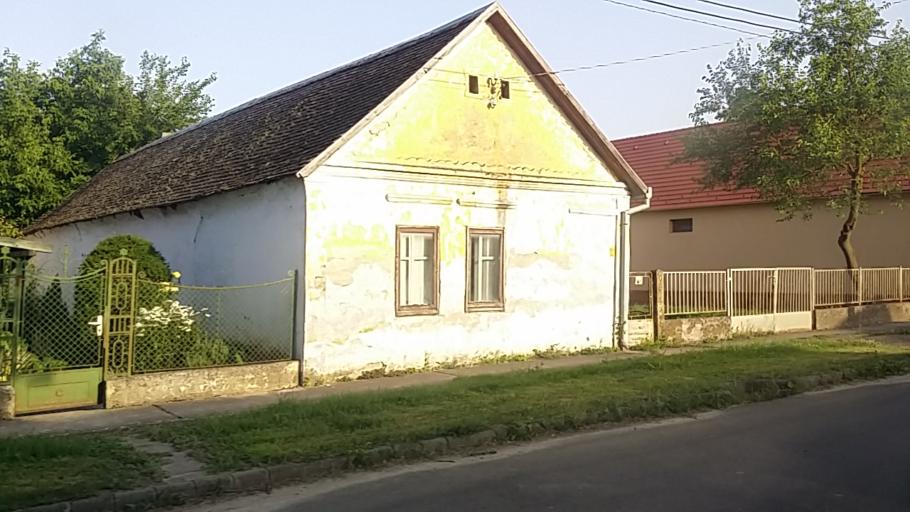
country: HU
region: Baranya
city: Villany
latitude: 45.8719
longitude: 18.4610
